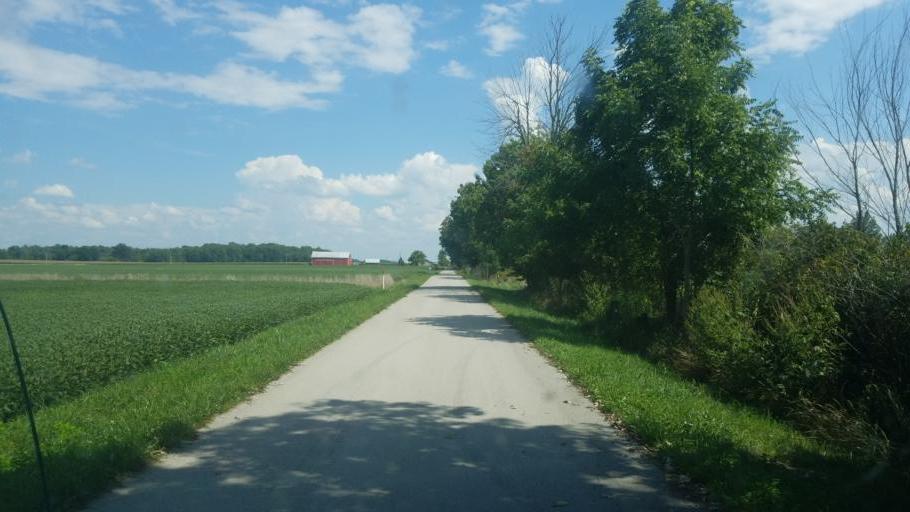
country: US
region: Ohio
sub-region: Hardin County
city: Forest
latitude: 40.8469
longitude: -83.4245
